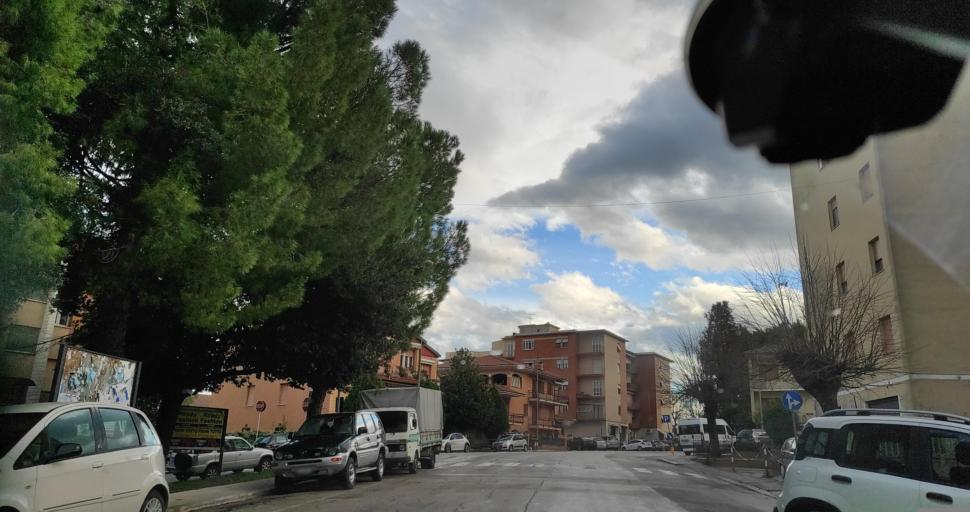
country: IT
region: The Marches
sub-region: Provincia di Macerata
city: Villa Potenza
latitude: 43.2992
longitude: 13.4295
